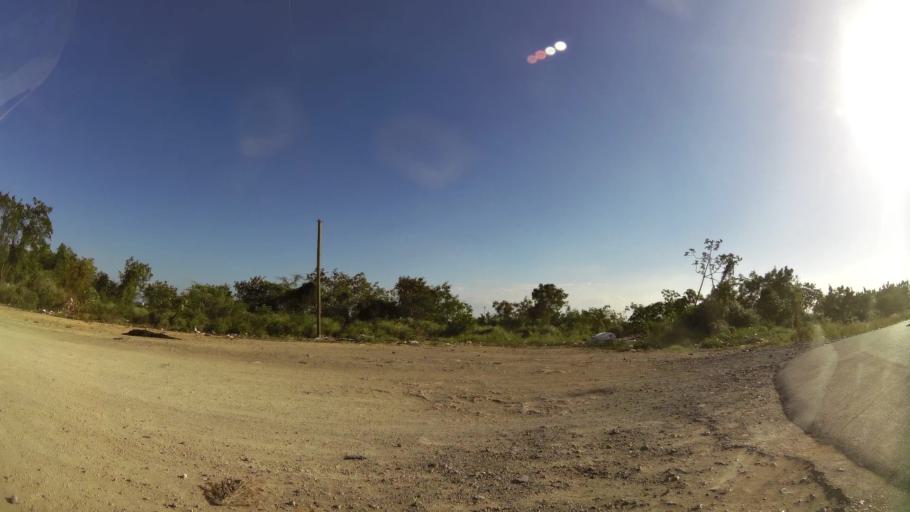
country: DO
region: Santo Domingo
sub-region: Santo Domingo
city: Santo Domingo Este
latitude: 18.4829
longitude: -69.8119
